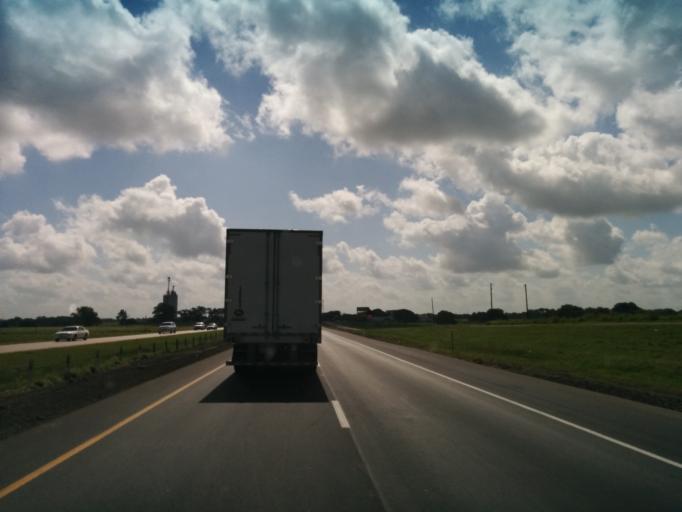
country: US
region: Texas
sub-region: Colorado County
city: Weimar
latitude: 29.6920
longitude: -96.7700
